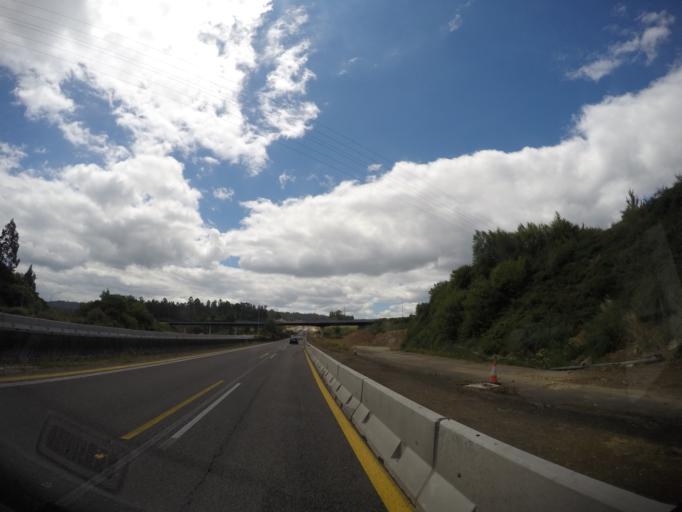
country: ES
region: Galicia
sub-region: Provincia da Coruna
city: Lousame
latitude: 42.8143
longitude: -8.7835
